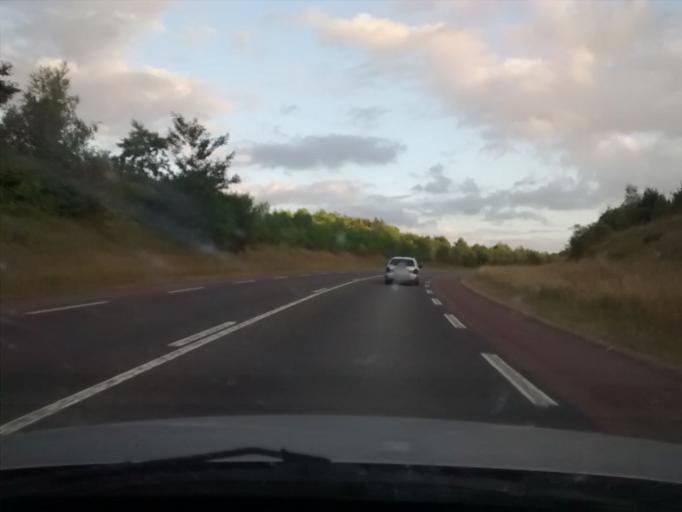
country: FR
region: Pays de la Loire
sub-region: Departement de la Sarthe
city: Saint-Saturnin
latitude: 48.0598
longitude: 0.1745
